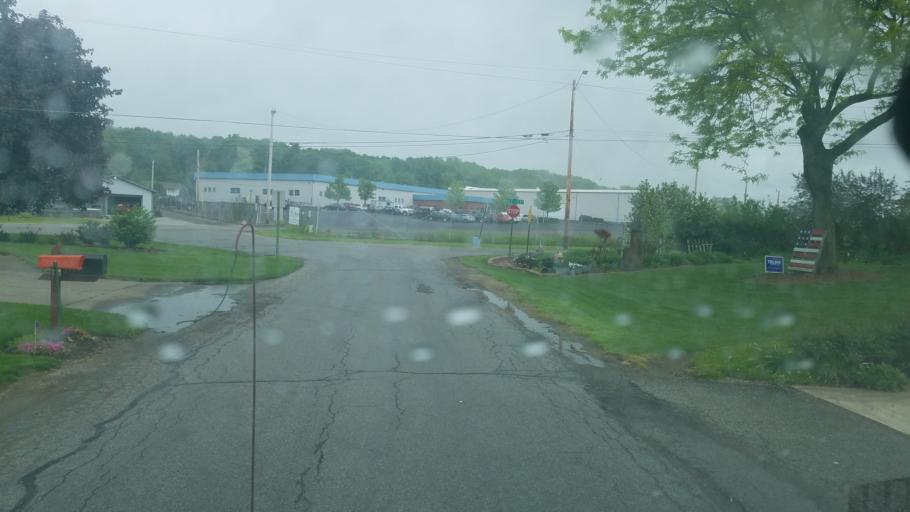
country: US
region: Ohio
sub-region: Wayne County
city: Apple Creek
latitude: 40.7499
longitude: -81.8294
